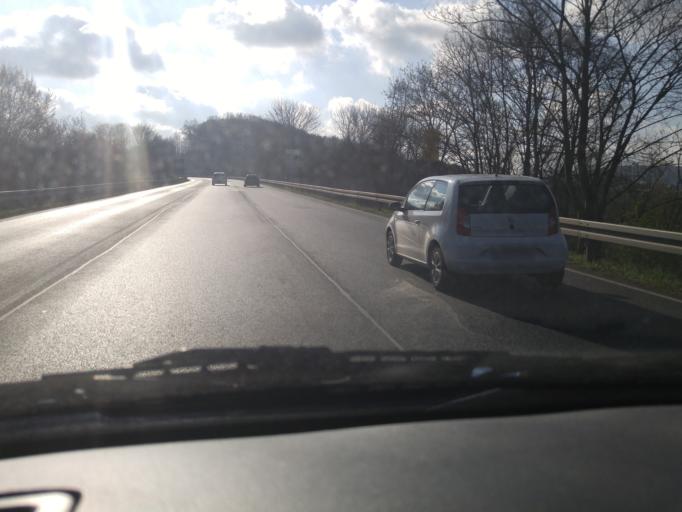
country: DE
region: Hesse
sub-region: Regierungsbezirk Kassel
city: Grossenluder
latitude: 50.5745
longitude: 9.5791
